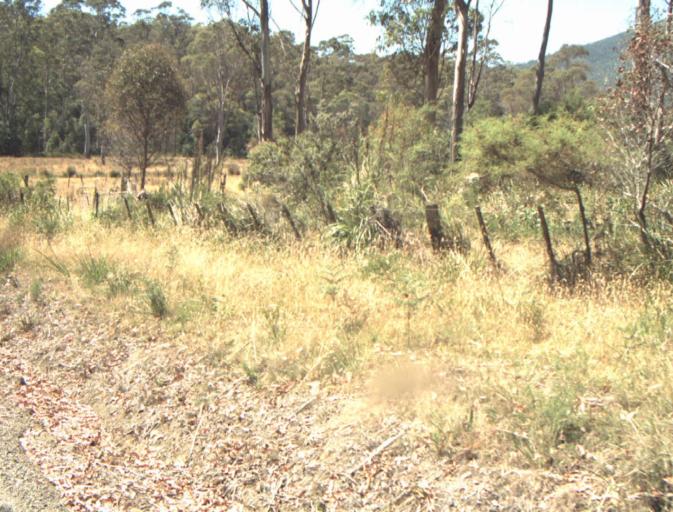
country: AU
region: Tasmania
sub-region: Launceston
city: Newstead
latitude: -41.3432
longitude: 147.3630
